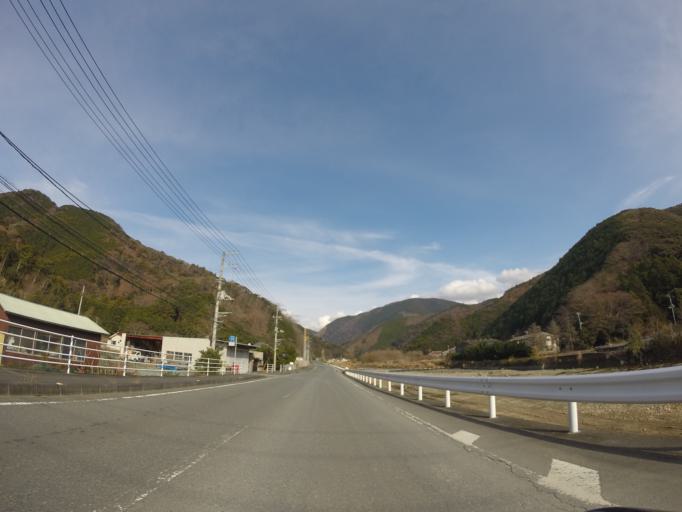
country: JP
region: Shizuoka
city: Heda
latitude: 34.7817
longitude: 138.7952
